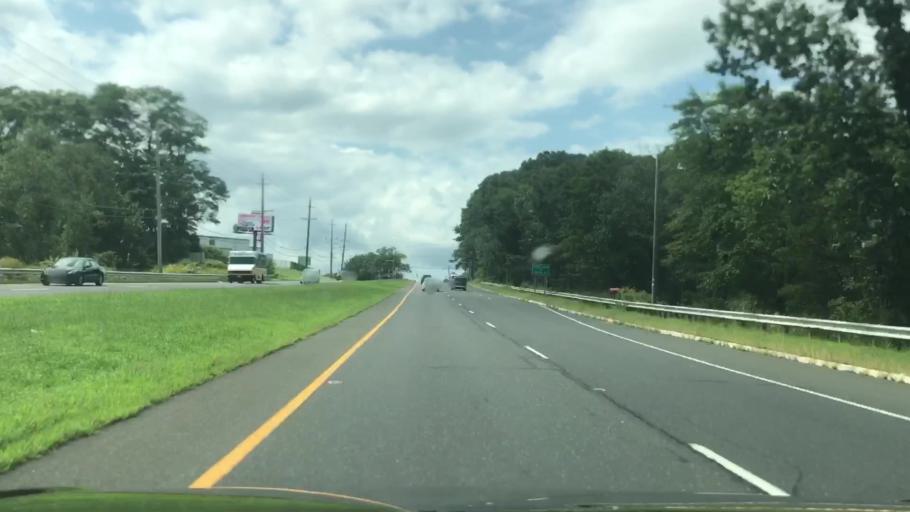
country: US
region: New Jersey
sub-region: Monmouth County
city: Wanamassa
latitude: 40.2298
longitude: -74.0561
